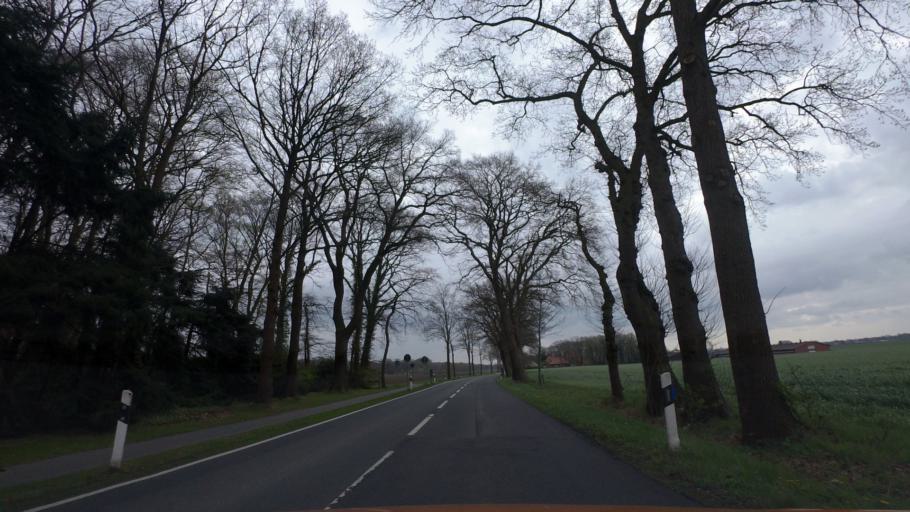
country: DE
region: Lower Saxony
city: Grossenkneten
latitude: 53.0087
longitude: 8.2572
